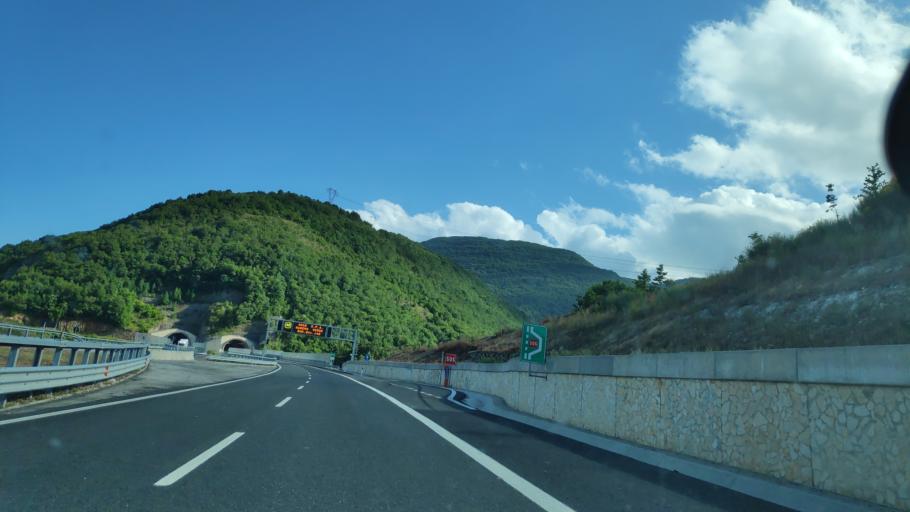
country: IT
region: Campania
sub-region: Provincia di Salerno
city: Casalbuono
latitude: 40.2170
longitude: 15.6718
